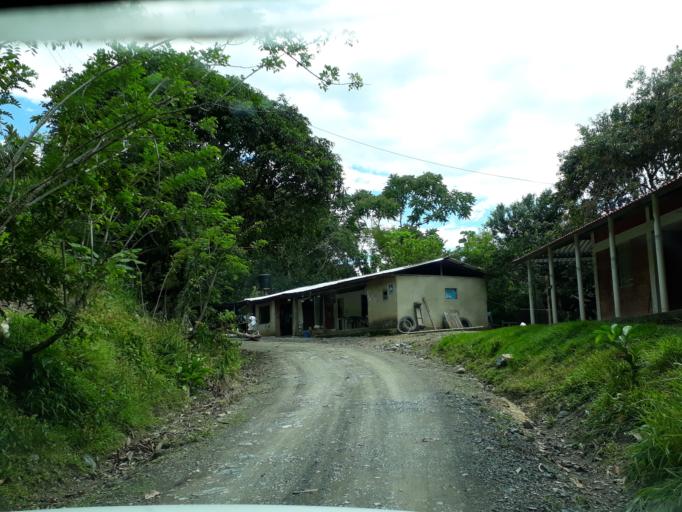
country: CO
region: Boyaca
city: Quipama
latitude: 5.4472
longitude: -74.1775
